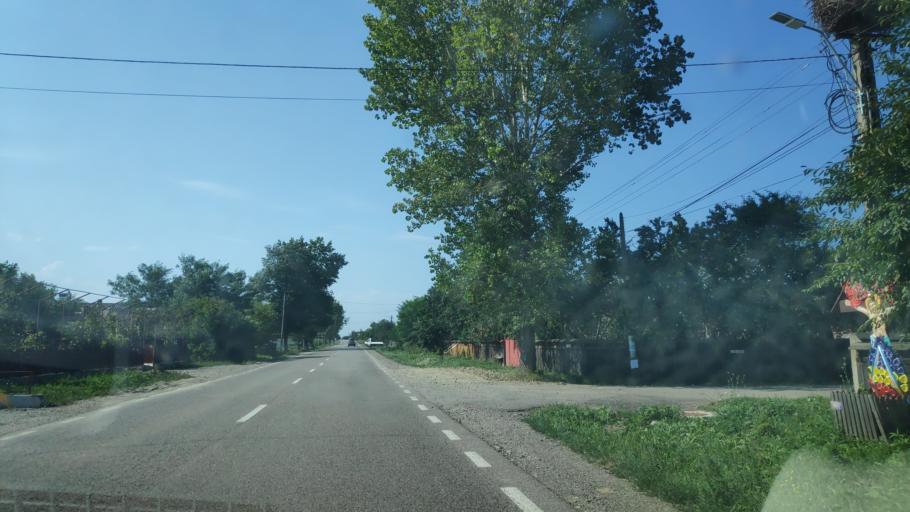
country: RO
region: Suceava
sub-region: Comuna Boroaia
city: Boroaia
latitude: 47.3760
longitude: 26.3229
